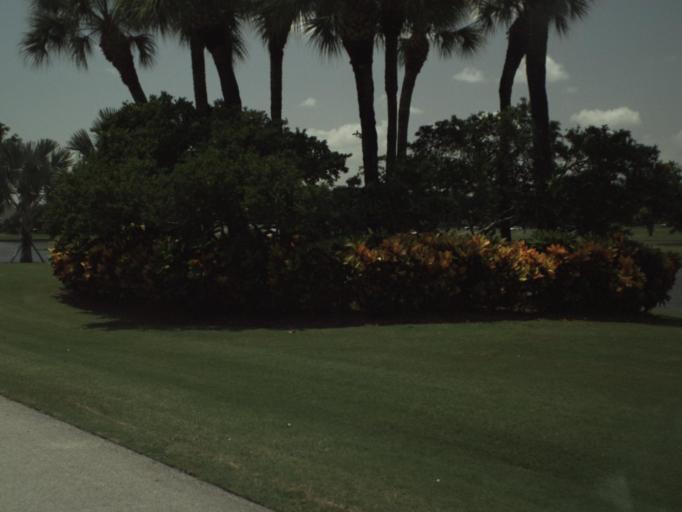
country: US
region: Florida
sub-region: Palm Beach County
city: Boca Pointe
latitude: 26.3393
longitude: -80.1538
